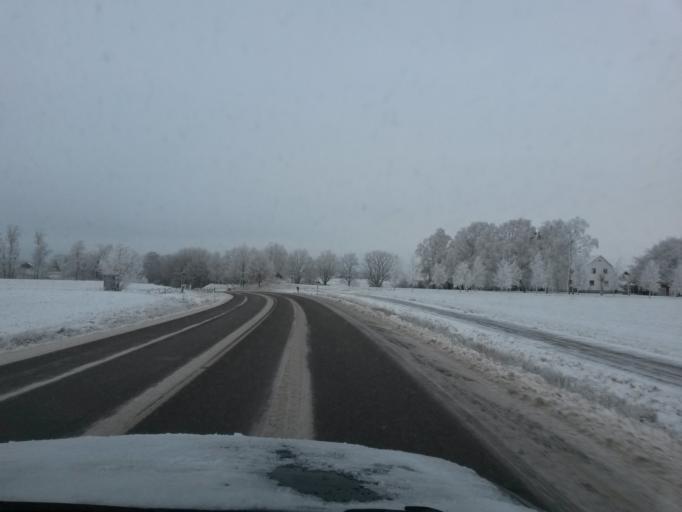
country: SE
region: Vaestra Goetaland
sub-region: Vara Kommun
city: Vara
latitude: 58.3081
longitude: 12.9534
